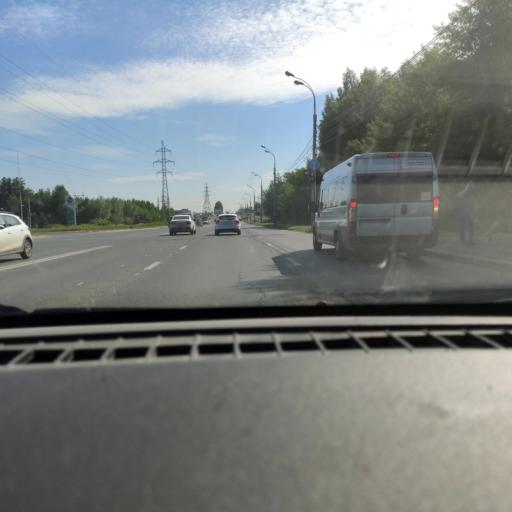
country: RU
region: Udmurtiya
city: Khokhryaki
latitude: 56.8980
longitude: 53.3016
